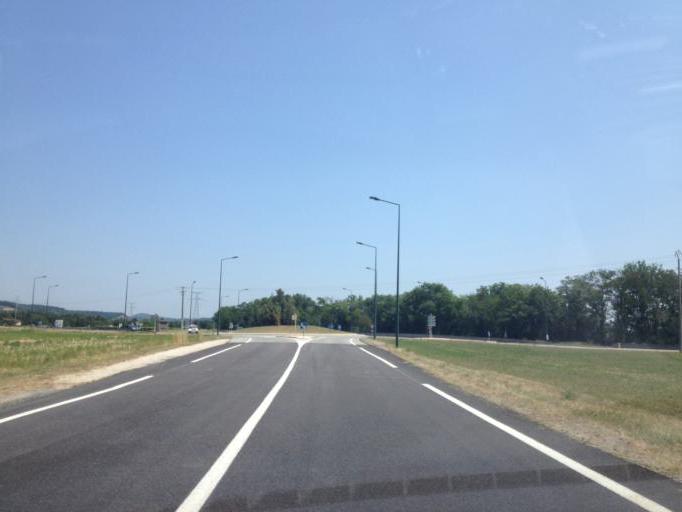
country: FR
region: Rhone-Alpes
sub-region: Departement de la Drome
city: Beaumont-Monteux
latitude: 45.0312
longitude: 4.9296
